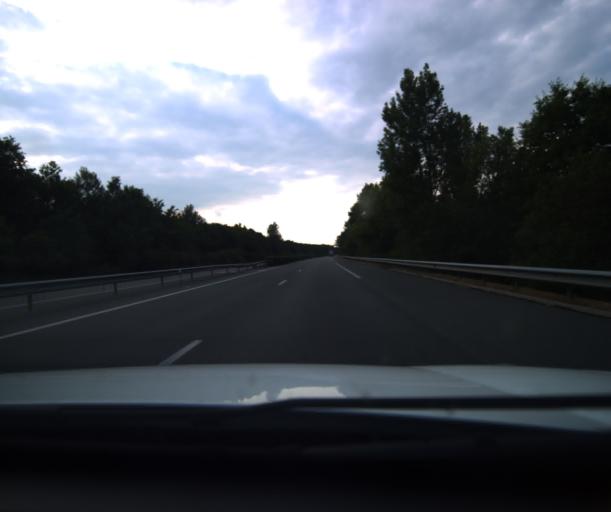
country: FR
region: Midi-Pyrenees
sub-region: Departement du Tarn-et-Garonne
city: Montech
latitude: 43.9885
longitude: 1.2387
